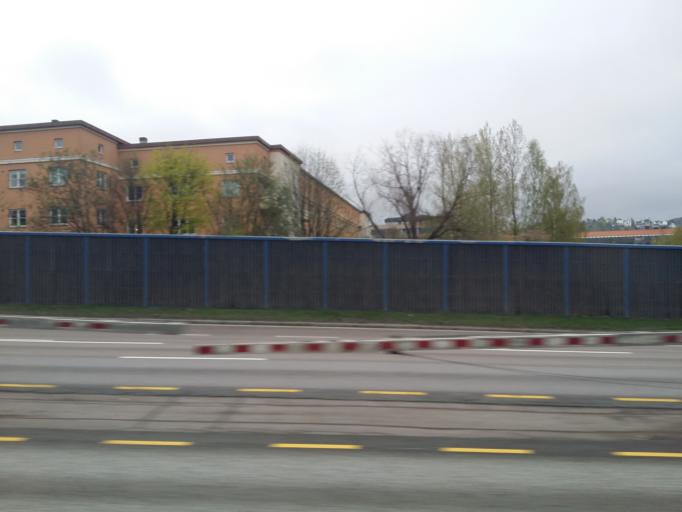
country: NO
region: Oslo
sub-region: Oslo
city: Oslo
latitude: 59.9112
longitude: 10.7946
